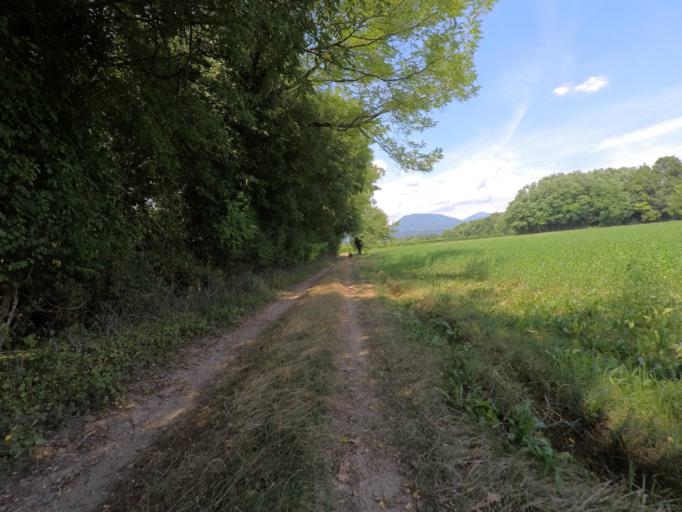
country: IT
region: Friuli Venezia Giulia
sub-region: Provincia di Pordenone
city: Lestans
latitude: 46.1477
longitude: 12.9079
